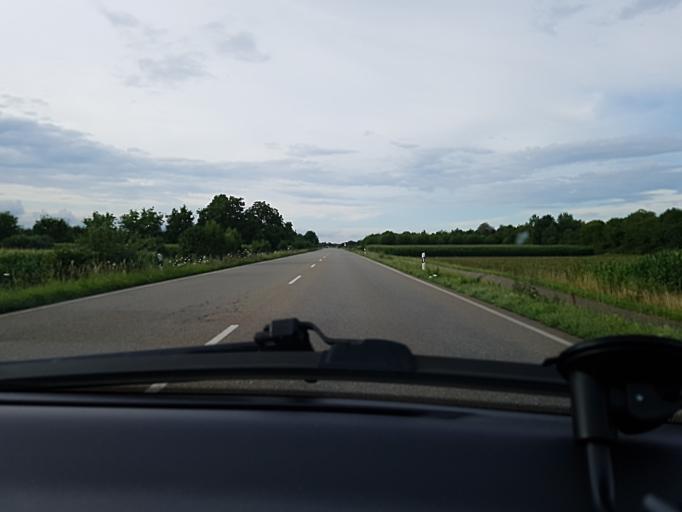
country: DE
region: Baden-Wuerttemberg
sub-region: Freiburg Region
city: Offenburg
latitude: 48.5064
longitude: 7.9594
